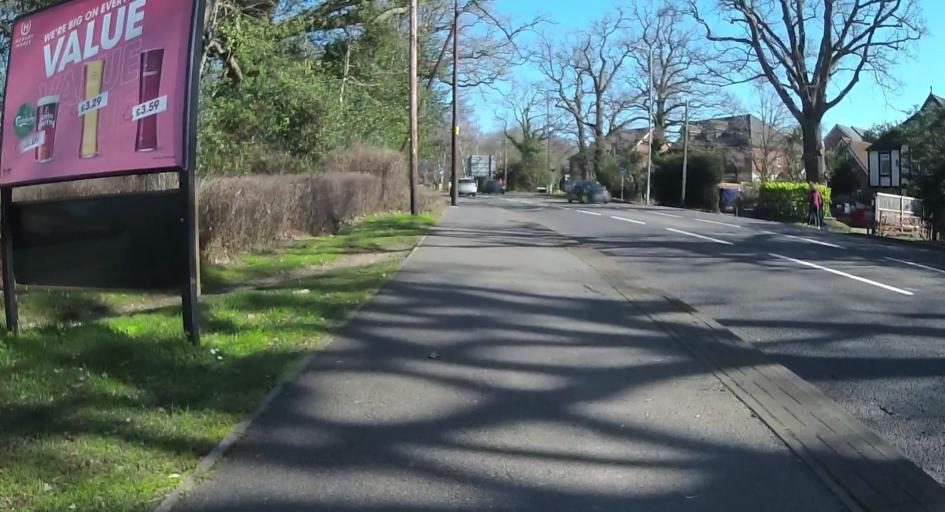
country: GB
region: England
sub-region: Bracknell Forest
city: Bracknell
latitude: 51.4132
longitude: -0.7305
